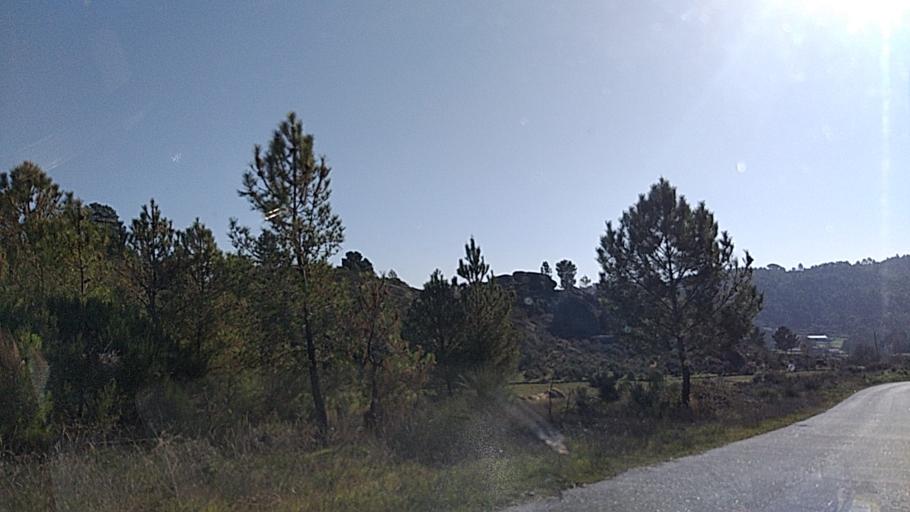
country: PT
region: Guarda
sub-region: Celorico da Beira
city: Celorico da Beira
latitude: 40.6851
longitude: -7.4140
